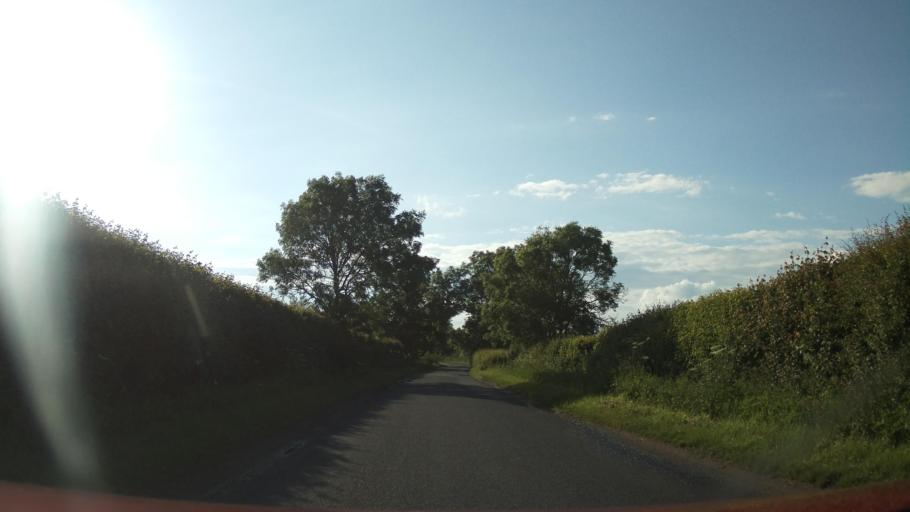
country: GB
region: England
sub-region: Lincolnshire
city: Navenby
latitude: 53.1162
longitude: -0.6216
